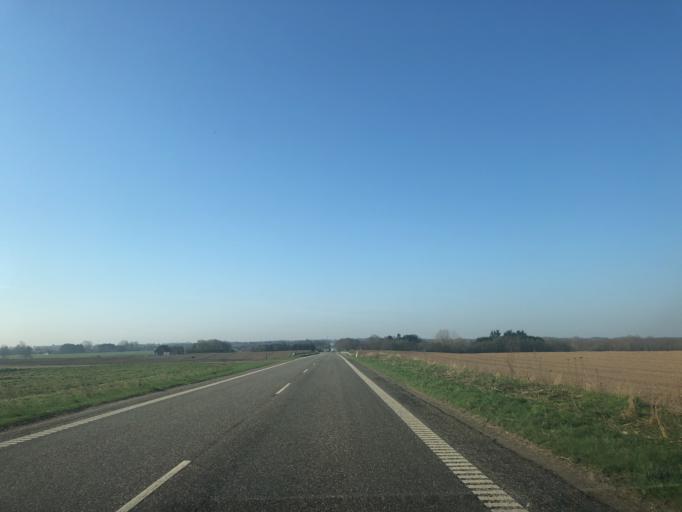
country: DK
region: Zealand
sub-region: Faxe Kommune
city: Ronnede
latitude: 55.2783
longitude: 12.0320
